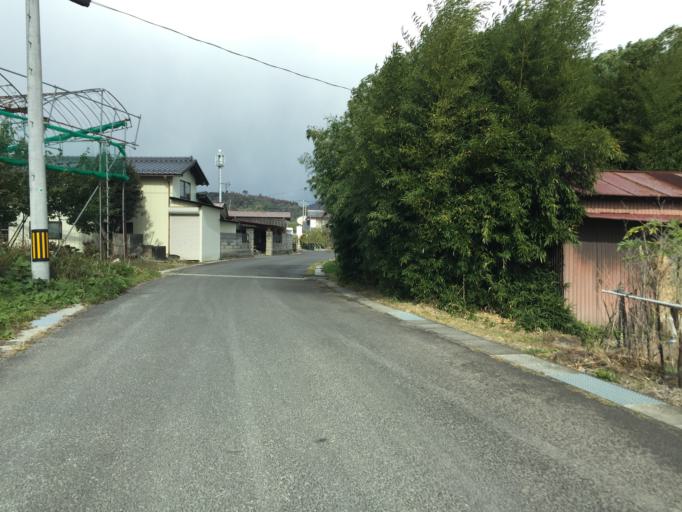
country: JP
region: Fukushima
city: Fukushima-shi
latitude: 37.8171
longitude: 140.4388
